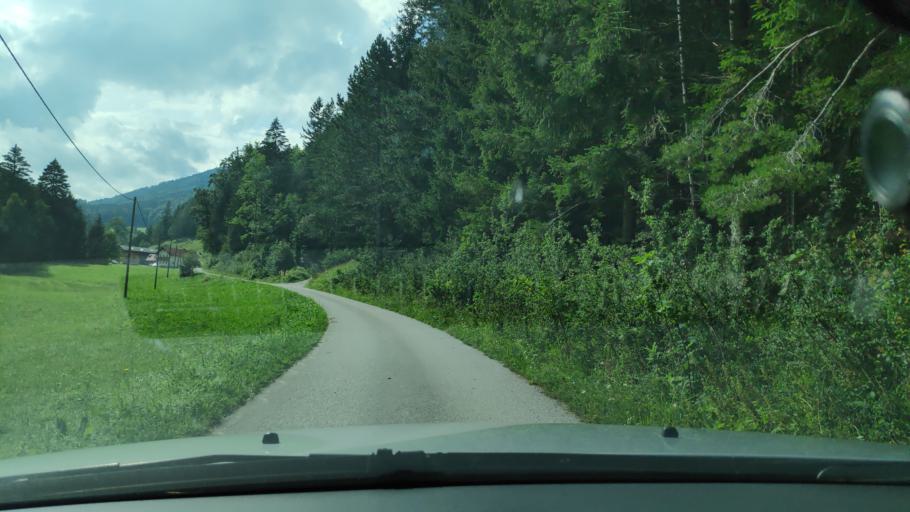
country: AT
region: Lower Austria
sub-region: Politischer Bezirk Wiener Neustadt
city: Miesenbach
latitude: 47.8368
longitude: 15.9590
